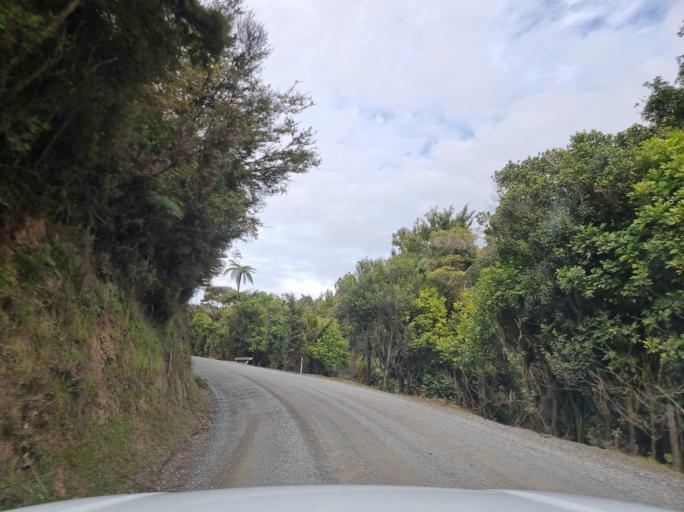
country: NZ
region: Northland
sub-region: Whangarei
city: Ruakaka
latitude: -36.0479
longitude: 174.4067
